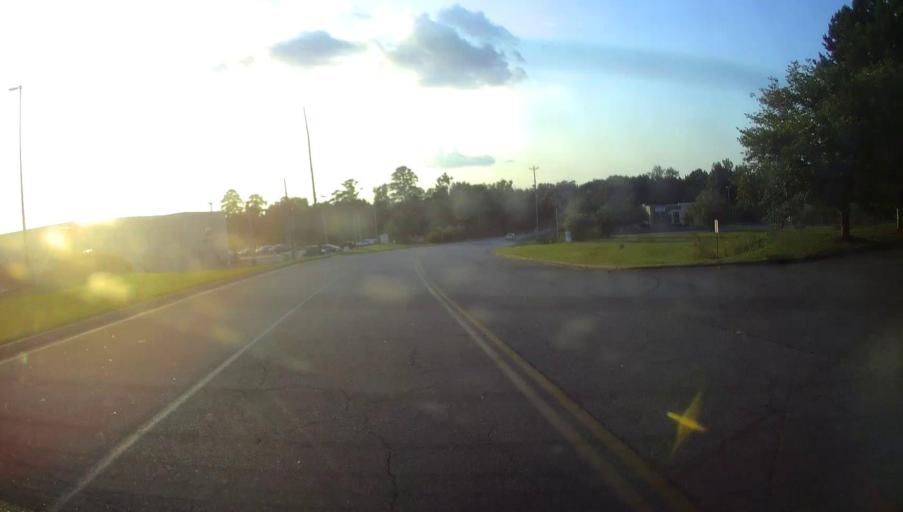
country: US
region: Georgia
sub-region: Bibb County
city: Macon
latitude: 32.9199
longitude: -83.7063
